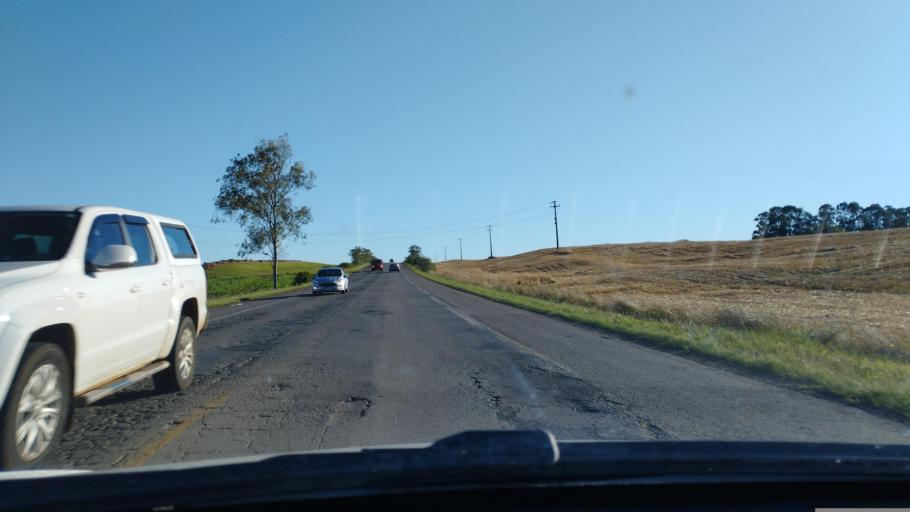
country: BR
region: Rio Grande do Sul
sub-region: Julio De Castilhos
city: Julio de Castilhos
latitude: -29.4227
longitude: -53.6728
